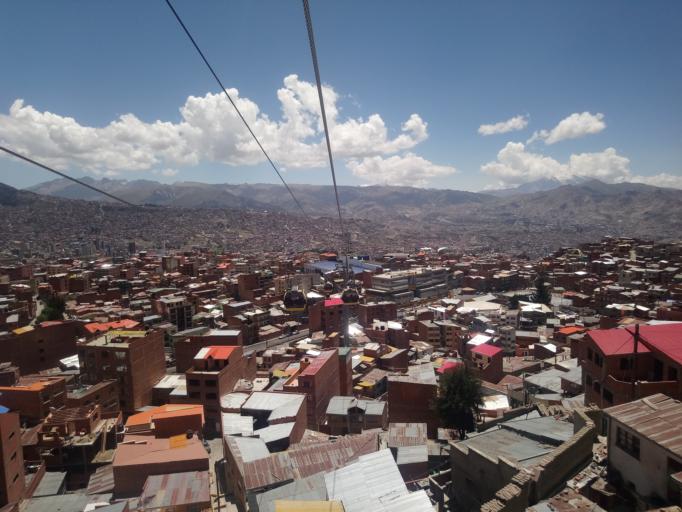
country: BO
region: La Paz
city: La Paz
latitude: -16.5154
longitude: -68.1425
